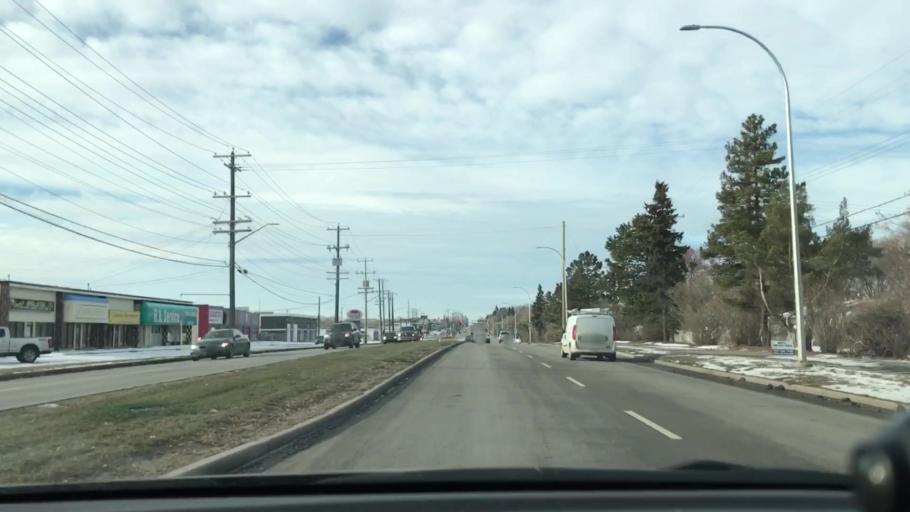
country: CA
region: Alberta
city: Edmonton
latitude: 53.4999
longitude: -113.4628
